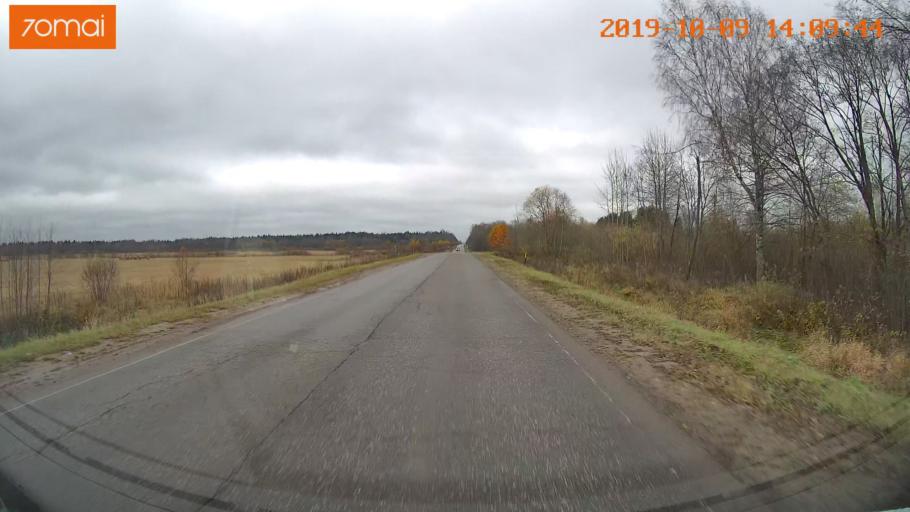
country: RU
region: Kostroma
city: Buy
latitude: 58.4808
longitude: 41.4592
